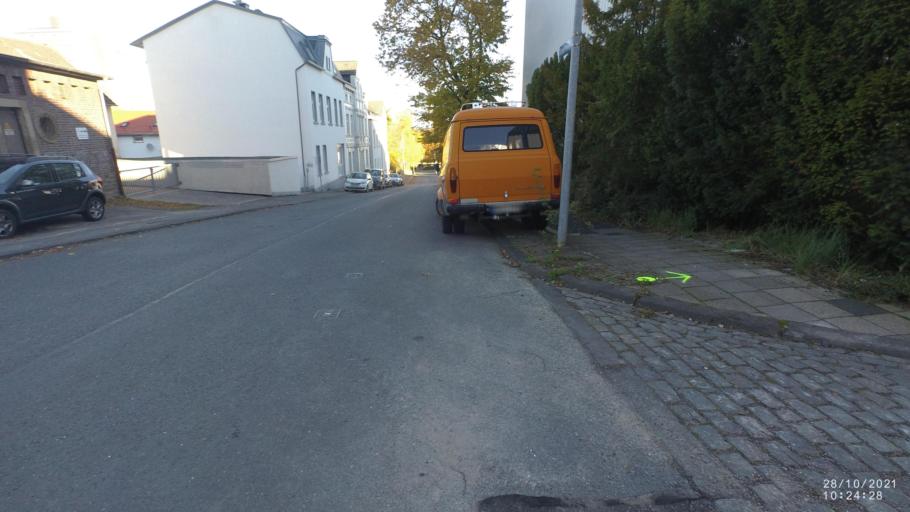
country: DE
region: North Rhine-Westphalia
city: Iserlohn
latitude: 51.3712
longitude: 7.7082
